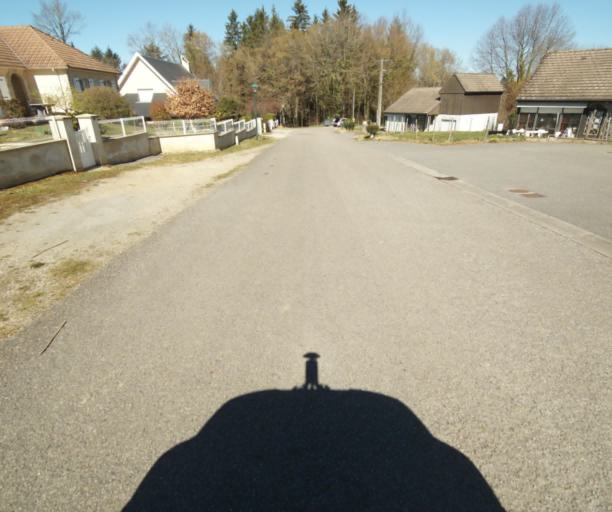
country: FR
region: Limousin
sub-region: Departement de la Correze
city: Chamboulive
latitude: 45.4273
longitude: 1.7034
